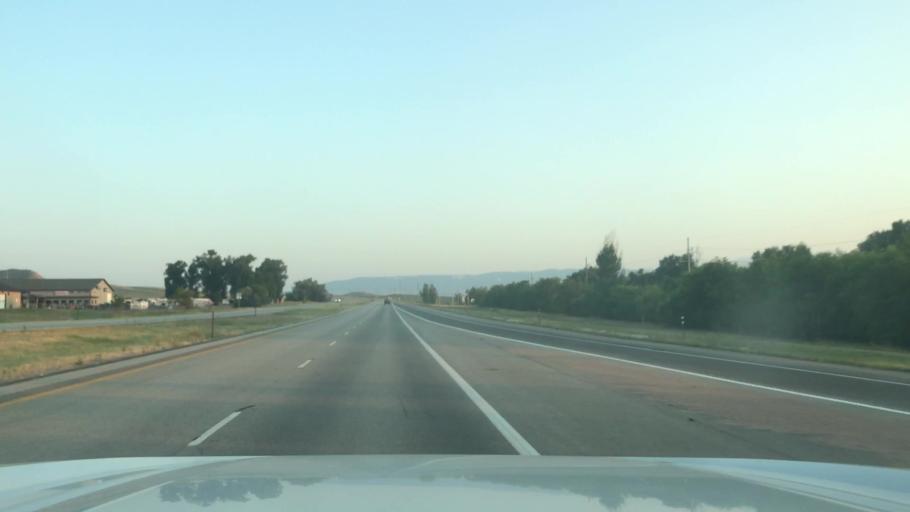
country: US
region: Wyoming
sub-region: Sheridan County
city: Sheridan
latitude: 44.7705
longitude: -106.9370
